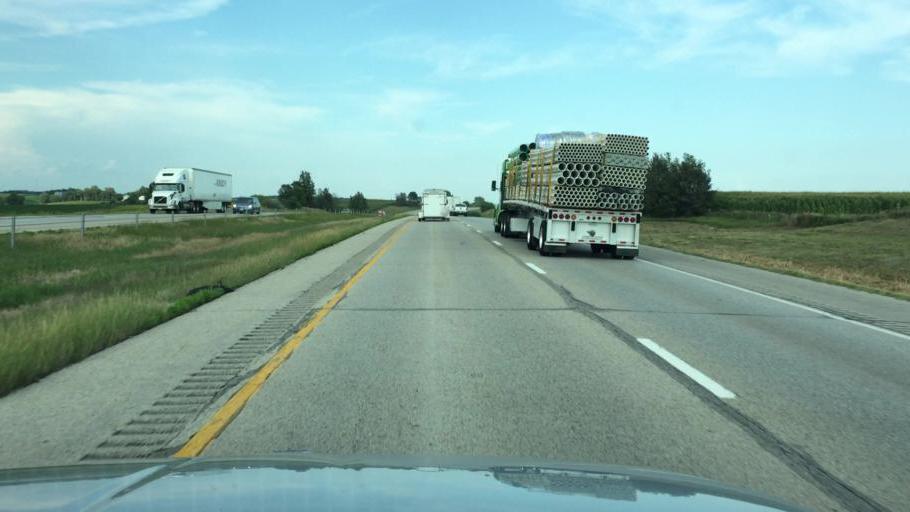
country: US
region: Iowa
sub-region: Johnson County
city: Tiffin
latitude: 41.6933
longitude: -91.7471
